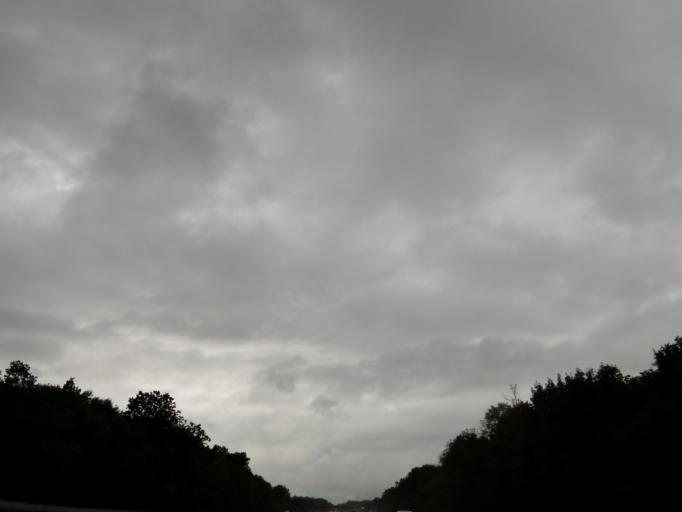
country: US
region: Illinois
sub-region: Jefferson County
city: Mount Vernon
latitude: 38.3509
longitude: -88.9869
